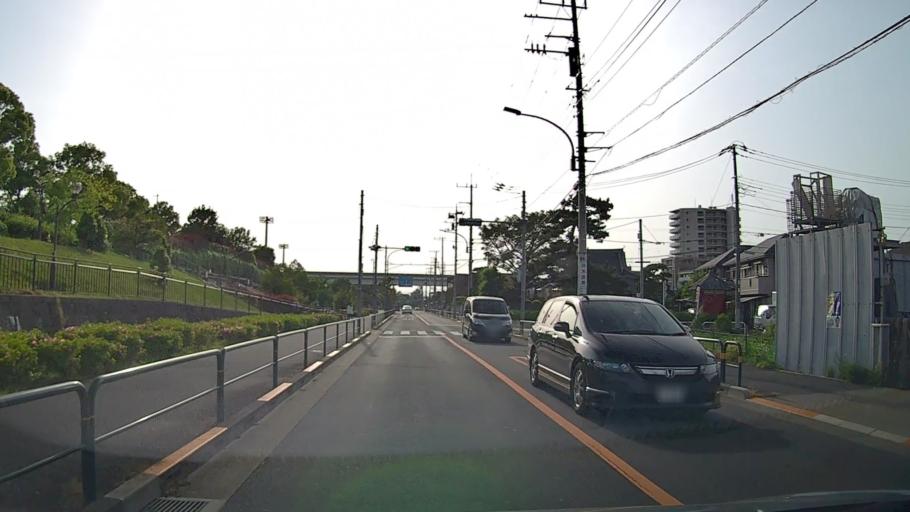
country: JP
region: Saitama
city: Soka
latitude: 35.8015
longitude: 139.7729
